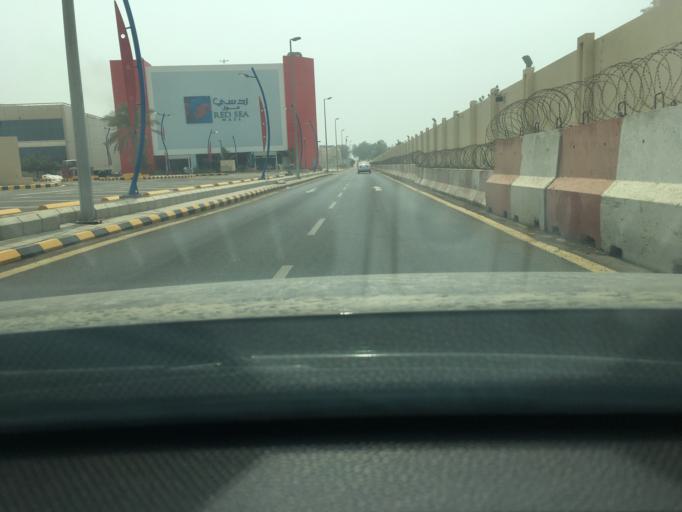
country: SA
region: Makkah
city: Jeddah
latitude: 21.6301
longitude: 39.1116
